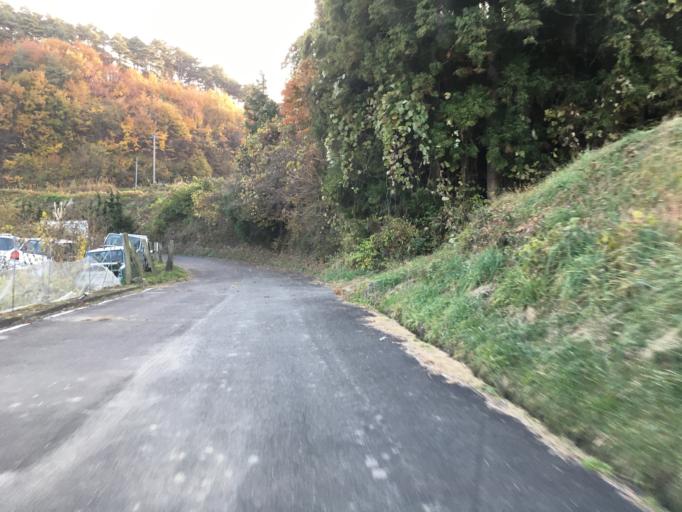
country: JP
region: Fukushima
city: Ishikawa
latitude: 37.2553
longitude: 140.5489
